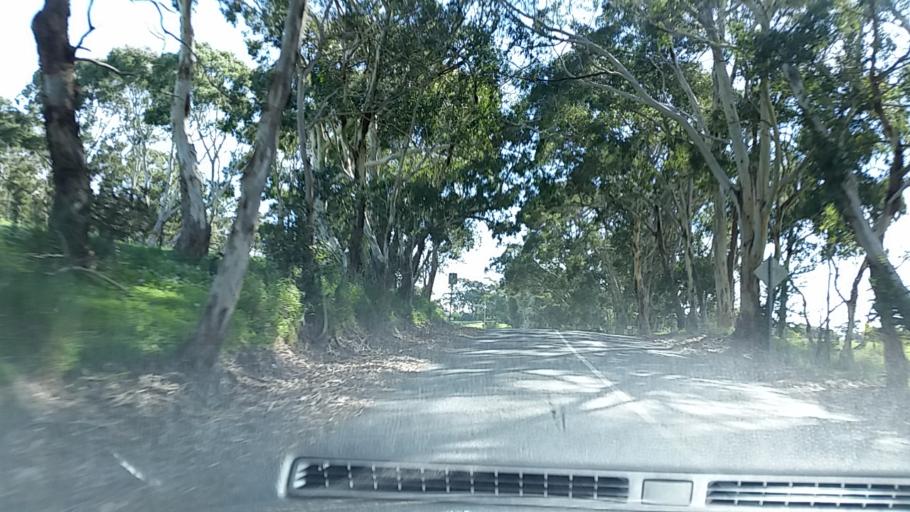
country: AU
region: South Australia
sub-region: Mount Barker
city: Little Hampton
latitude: -35.0798
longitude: 138.8242
